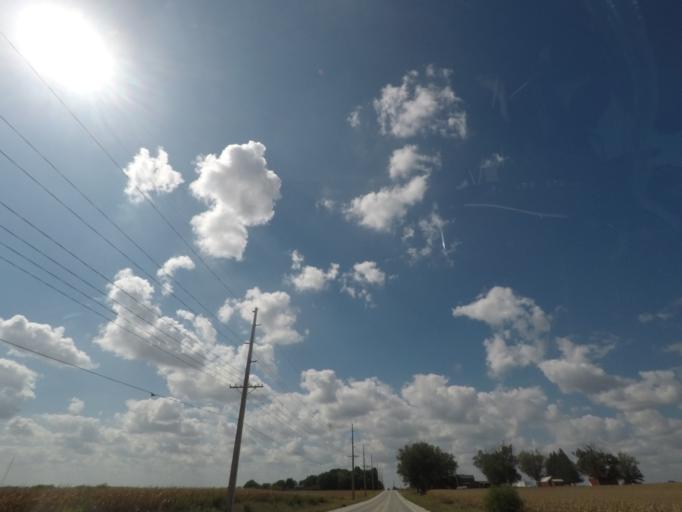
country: US
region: Iowa
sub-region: Story County
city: Ames
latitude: 42.0231
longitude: -93.5441
